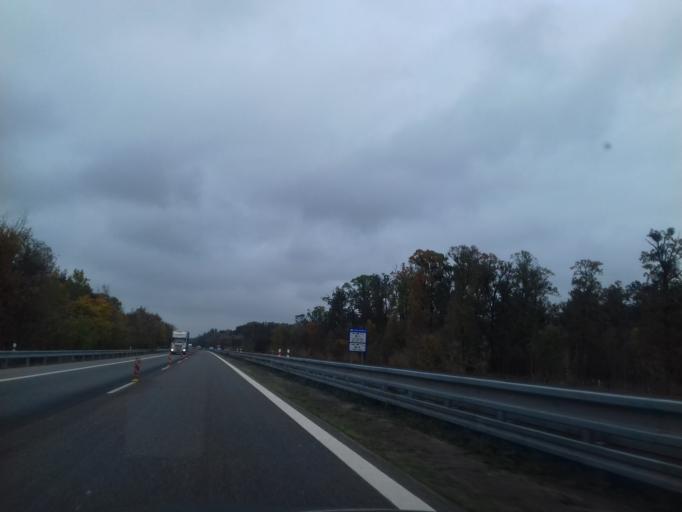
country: CZ
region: South Moravian
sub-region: Okres Breclav
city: Lanzhot
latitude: 48.7067
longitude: 16.9872
